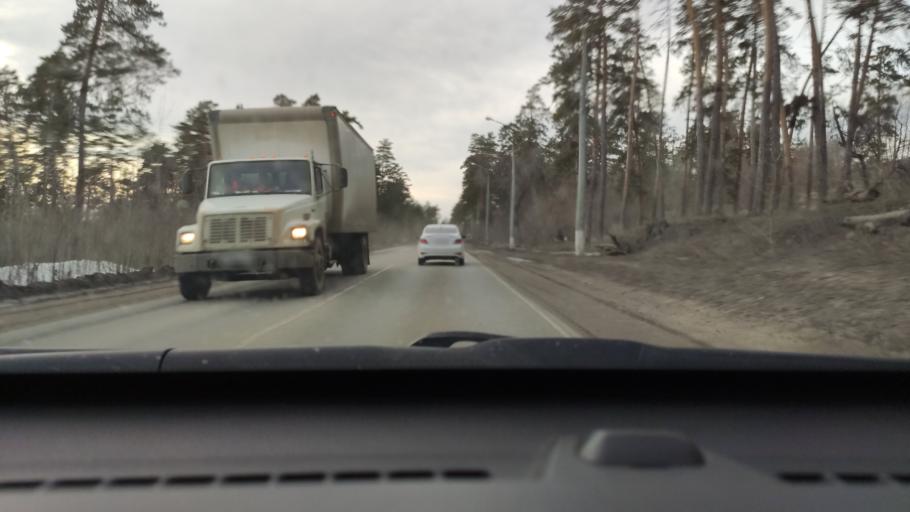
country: RU
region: Samara
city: Tol'yatti
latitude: 53.4682
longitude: 49.3834
